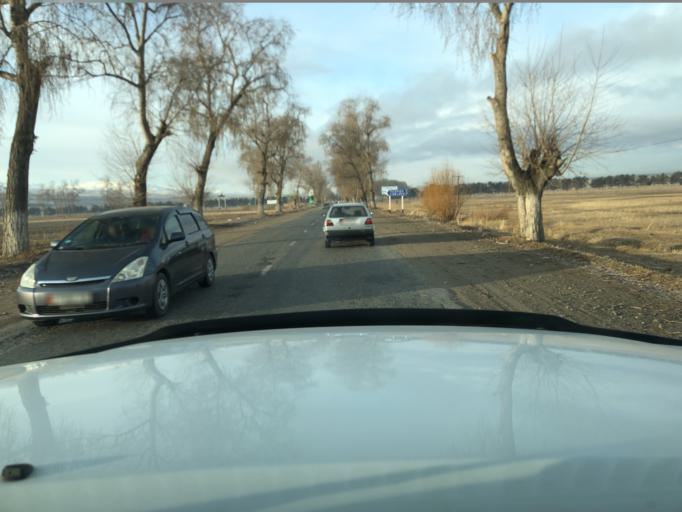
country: KG
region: Ysyk-Koel
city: Karakol
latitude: 42.4799
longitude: 78.3444
